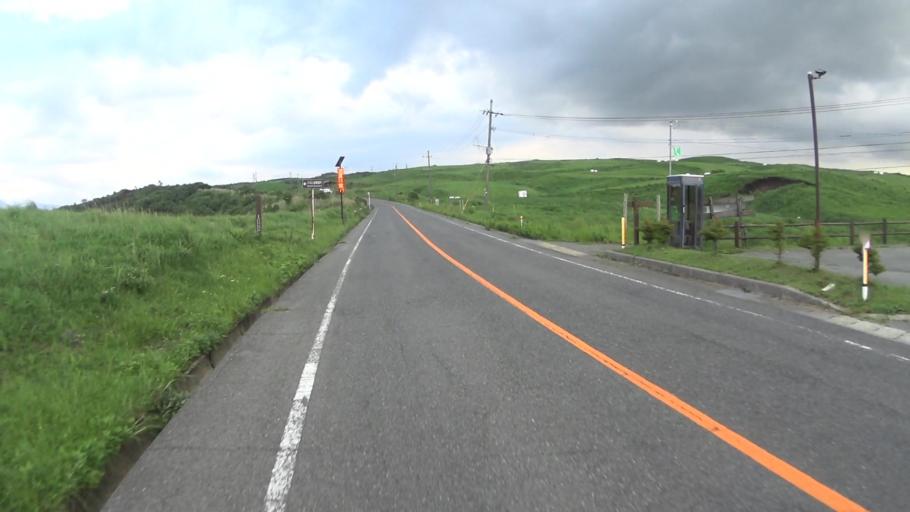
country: JP
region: Kumamoto
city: Aso
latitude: 32.9831
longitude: 131.0147
